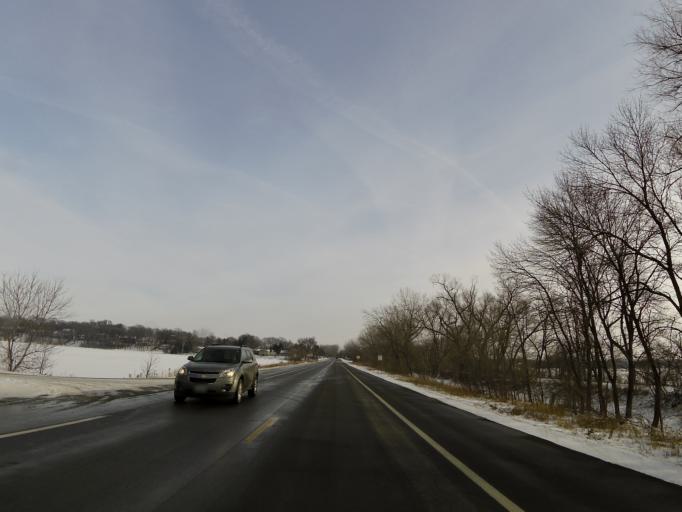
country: US
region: Minnesota
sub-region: McLeod County
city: Hutchinson
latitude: 44.8930
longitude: -94.4104
